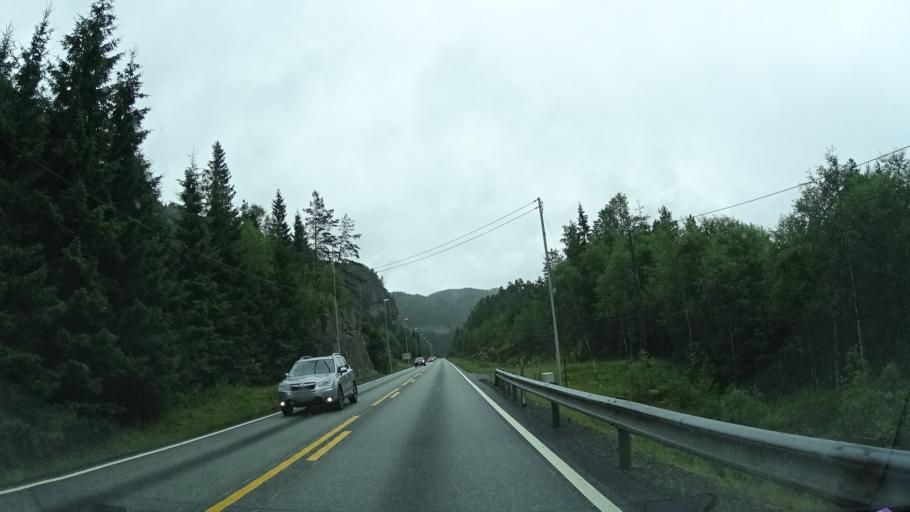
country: NO
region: Vest-Agder
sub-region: Flekkefjord
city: Flekkefjord
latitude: 58.3836
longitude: 6.6309
